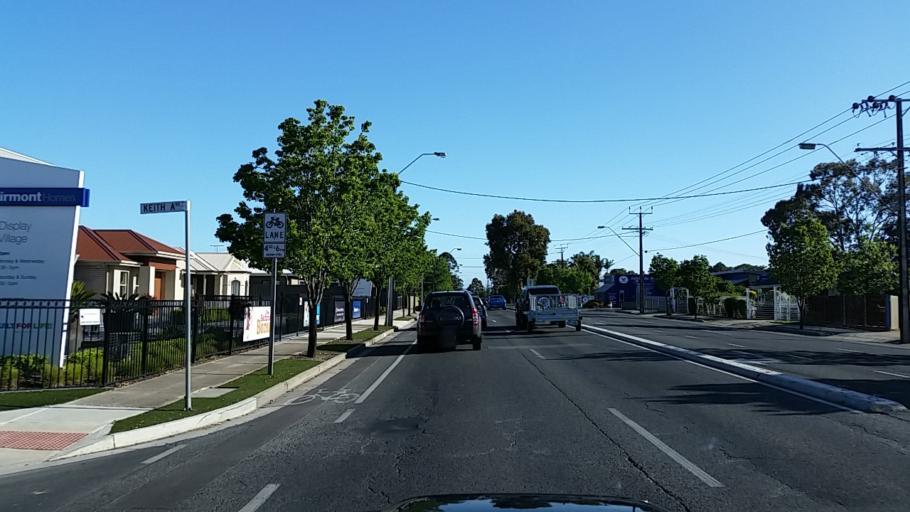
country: AU
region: South Australia
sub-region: City of West Torrens
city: Plympton
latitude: -34.9520
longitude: 138.5540
